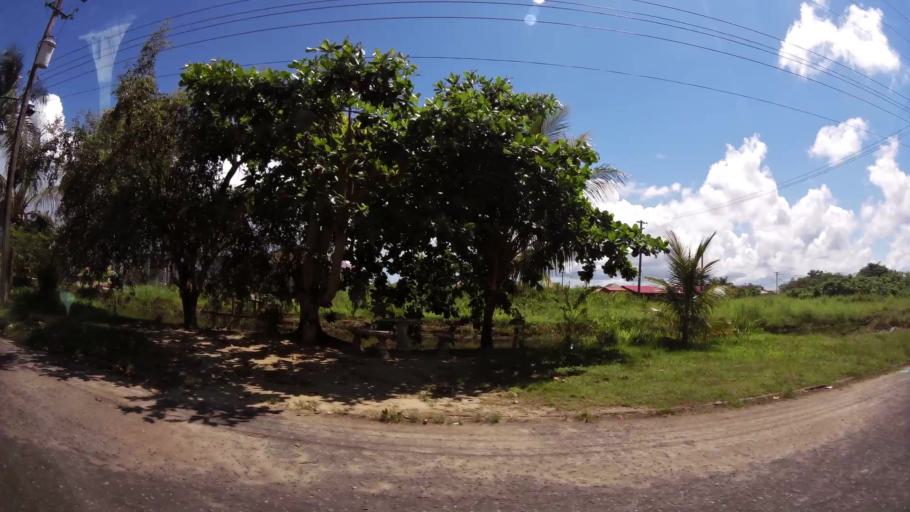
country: SR
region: Paramaribo
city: Paramaribo
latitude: 5.8655
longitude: -55.1403
